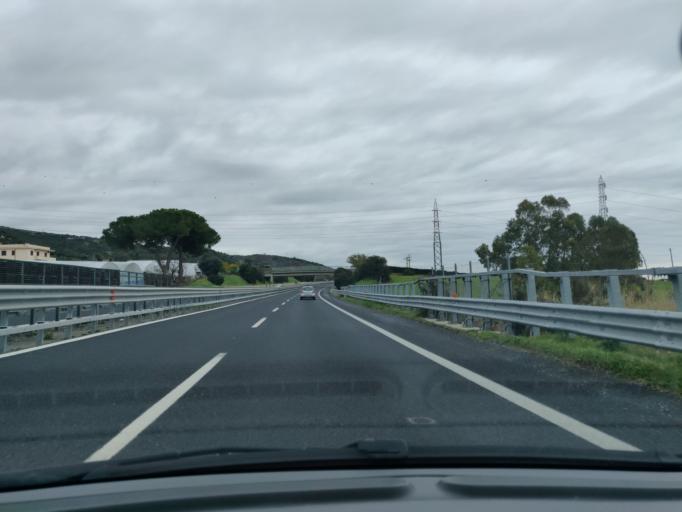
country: IT
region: Latium
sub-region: Citta metropolitana di Roma Capitale
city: Santa Marinella
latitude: 42.0440
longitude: 11.8905
